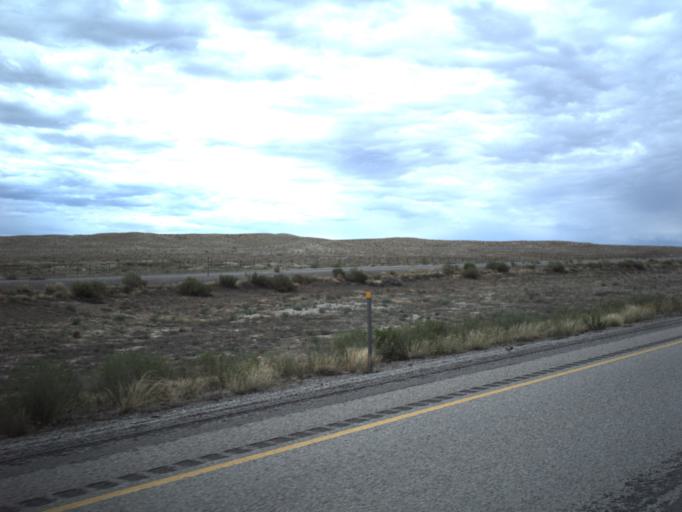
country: US
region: Utah
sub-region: Grand County
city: Moab
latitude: 38.9993
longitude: -109.3215
